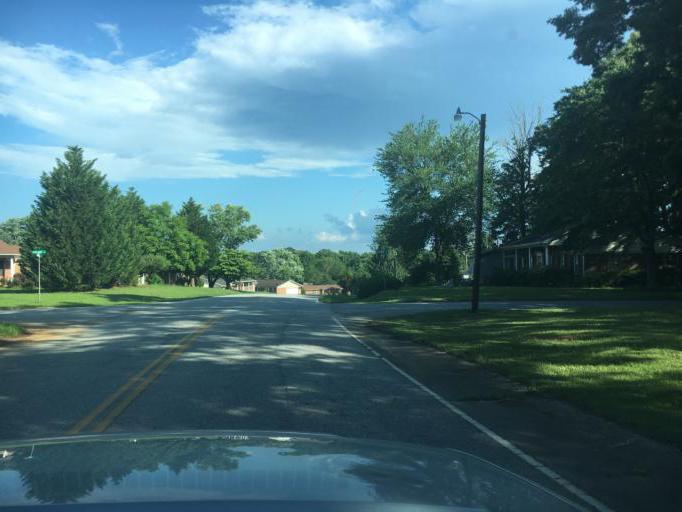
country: US
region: South Carolina
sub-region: Greenville County
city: Mauldin
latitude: 34.7906
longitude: -82.2988
